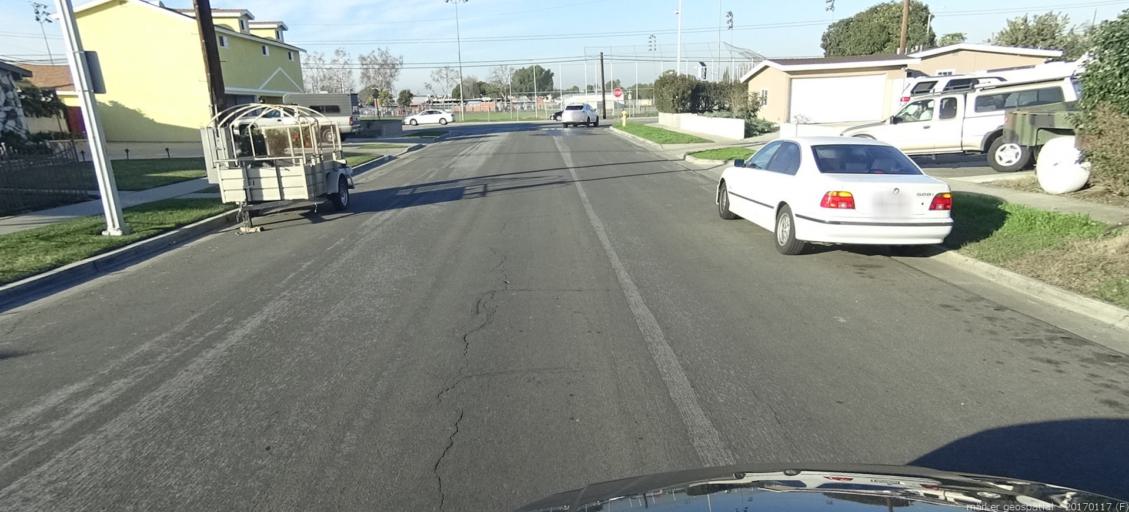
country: US
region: California
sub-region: Orange County
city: Midway City
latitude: 33.7369
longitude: -117.9854
